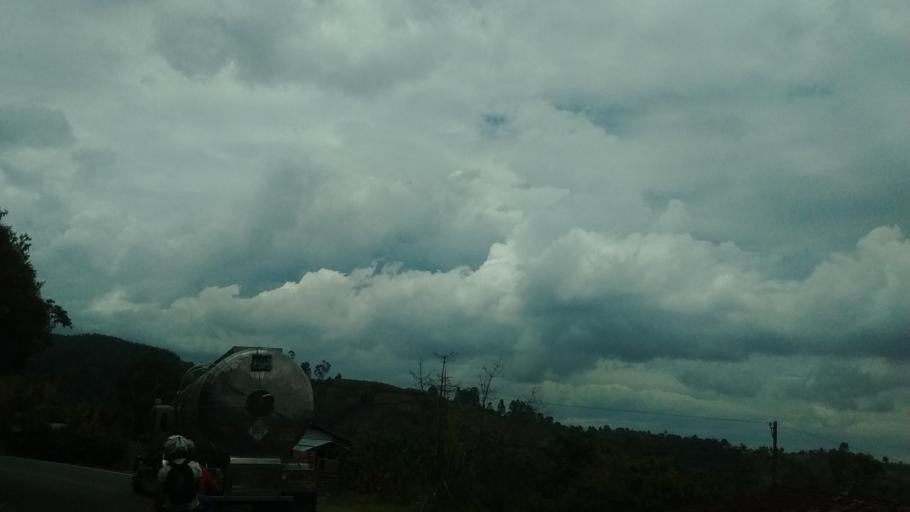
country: CO
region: Cauca
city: Rosas
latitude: 2.3091
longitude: -76.6861
